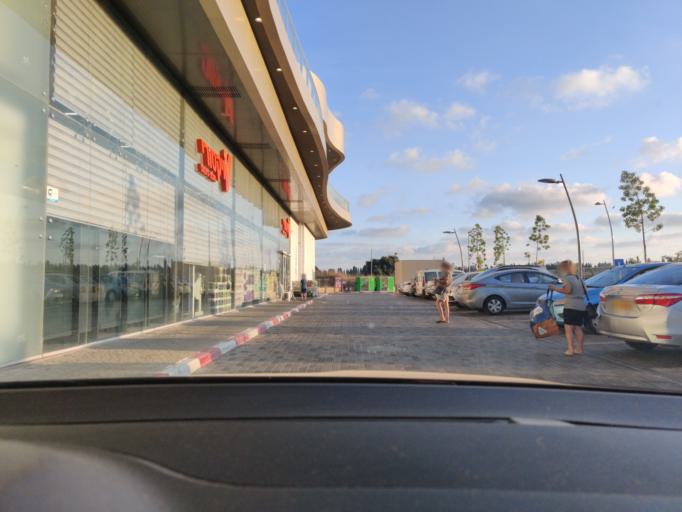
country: IL
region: Central District
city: Elyakhin
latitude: 32.4272
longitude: 34.9328
